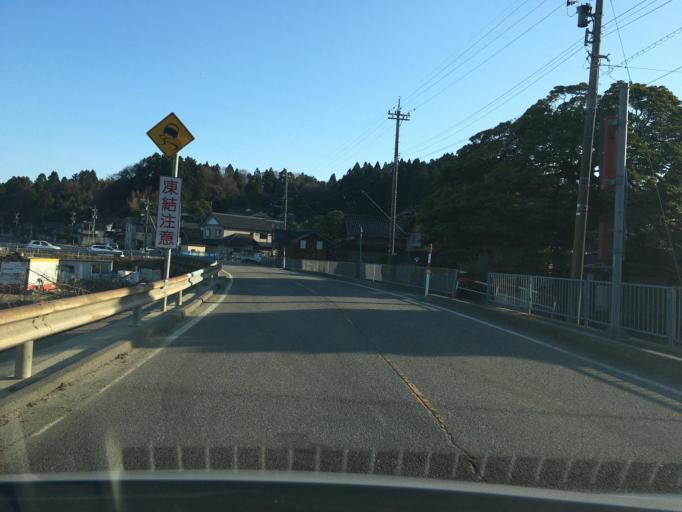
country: JP
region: Ishikawa
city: Nanao
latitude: 36.9779
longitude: 137.0498
